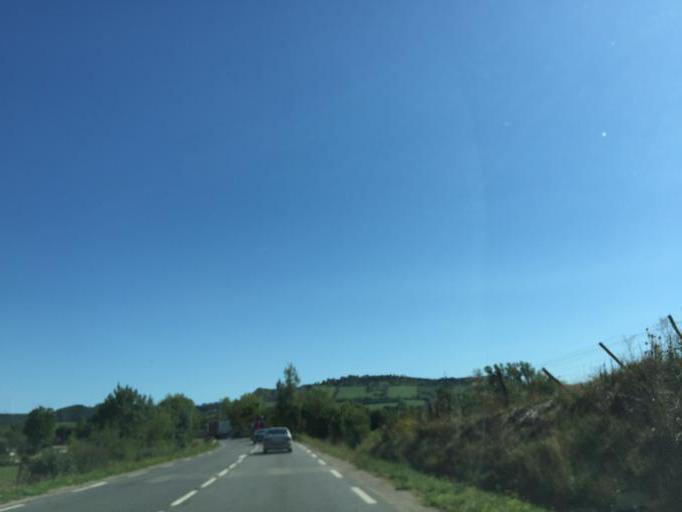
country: FR
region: Midi-Pyrenees
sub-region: Departement de l'Aveyron
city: Severac-le-Chateau
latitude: 44.3364
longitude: 3.0283
